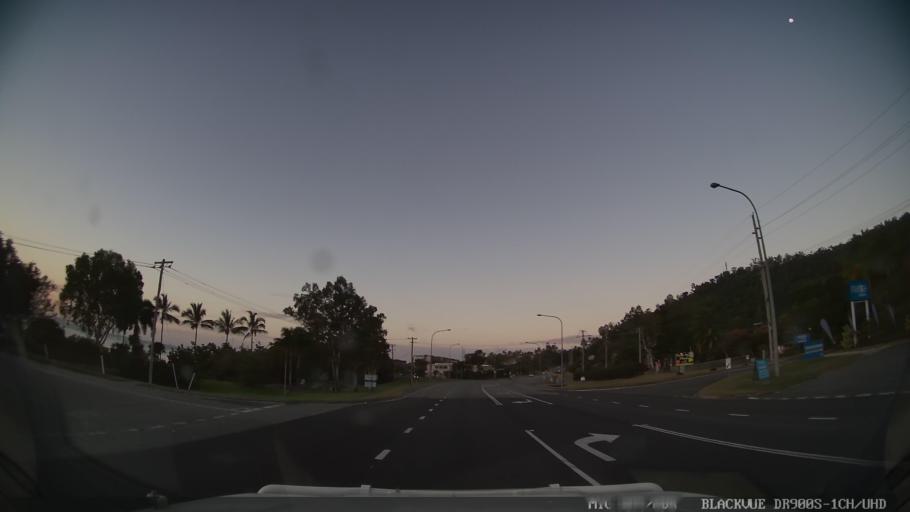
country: AU
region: Queensland
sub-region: Whitsunday
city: Proserpine
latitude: -20.2745
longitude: 148.7029
